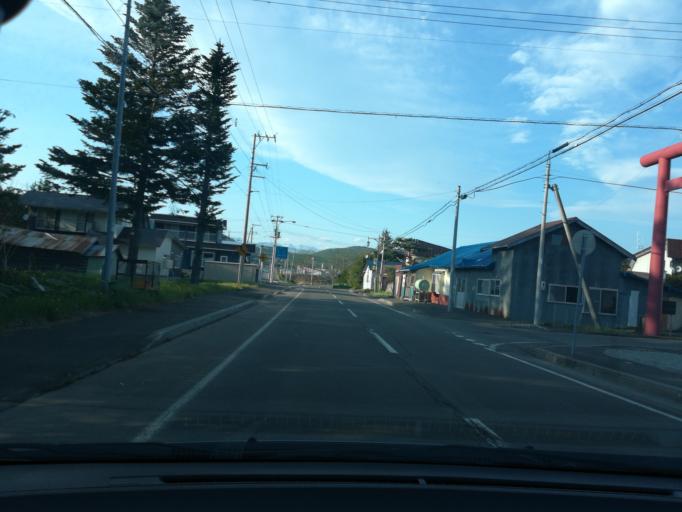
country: JP
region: Hokkaido
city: Shimo-furano
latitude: 43.1602
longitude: 142.5669
